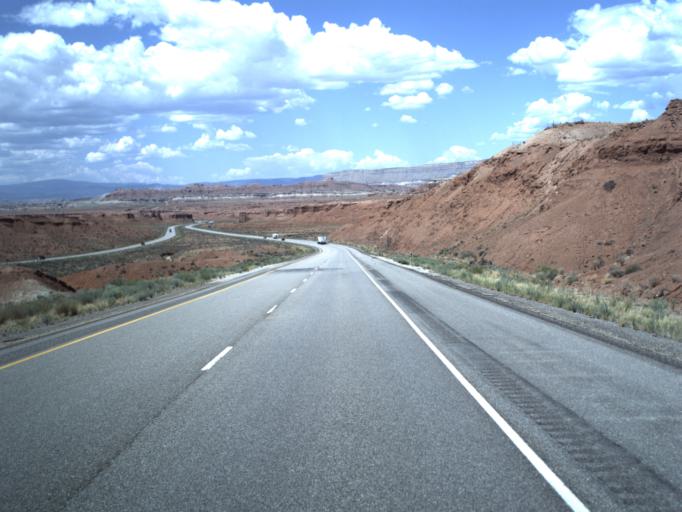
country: US
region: Utah
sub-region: Emery County
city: Ferron
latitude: 38.8476
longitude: -111.0257
